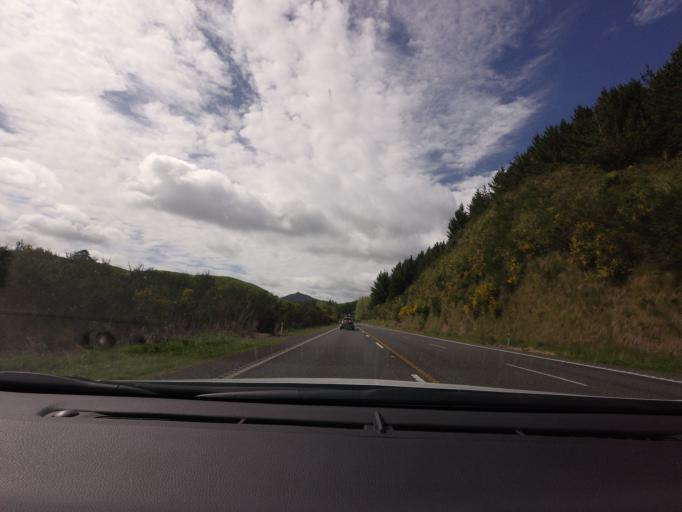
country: NZ
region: Bay of Plenty
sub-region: Rotorua District
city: Rotorua
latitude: -38.2925
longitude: 176.3544
